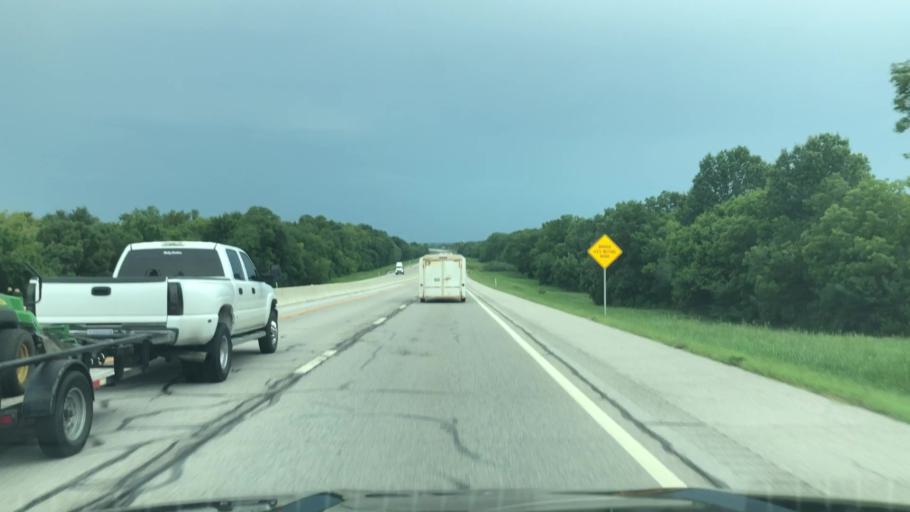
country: US
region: Oklahoma
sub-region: Rogers County
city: Chelsea
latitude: 36.4582
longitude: -95.3536
